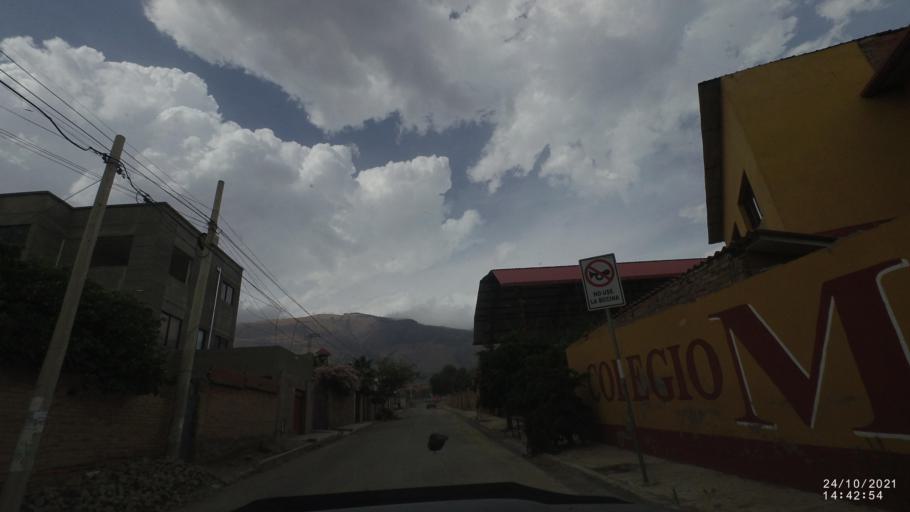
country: BO
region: Cochabamba
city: Cochabamba
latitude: -17.3499
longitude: -66.1770
